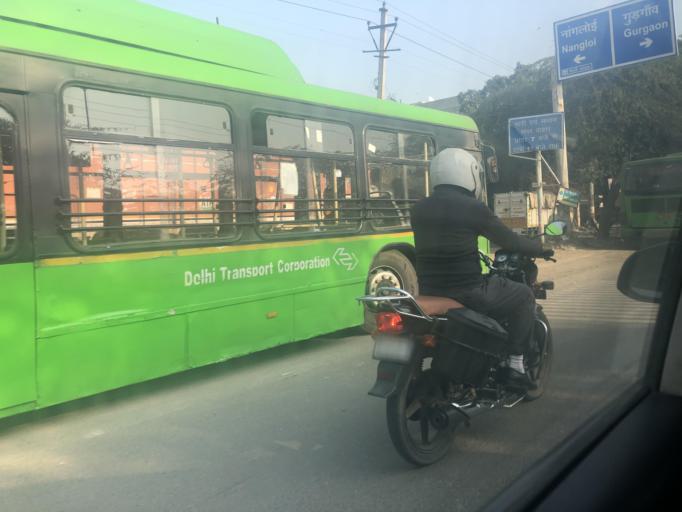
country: IN
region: Haryana
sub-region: Jhajjar
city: Bahadurgarh
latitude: 28.6195
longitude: 76.9738
